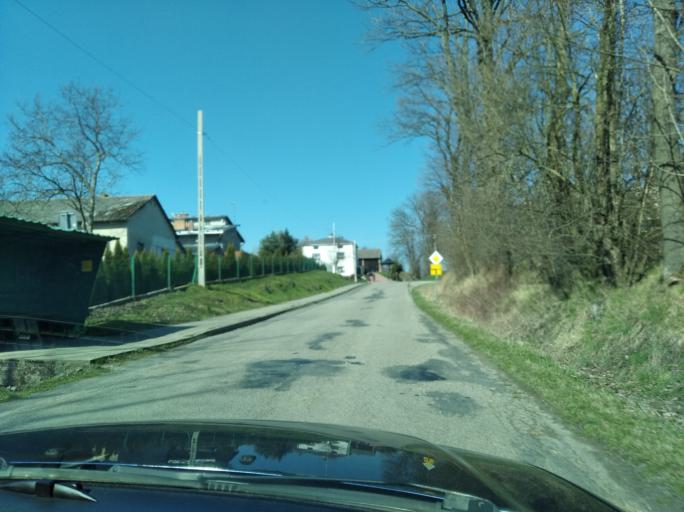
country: PL
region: Subcarpathian Voivodeship
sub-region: Powiat jaroslawski
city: Jodlowka
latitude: 49.9280
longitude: 22.4639
